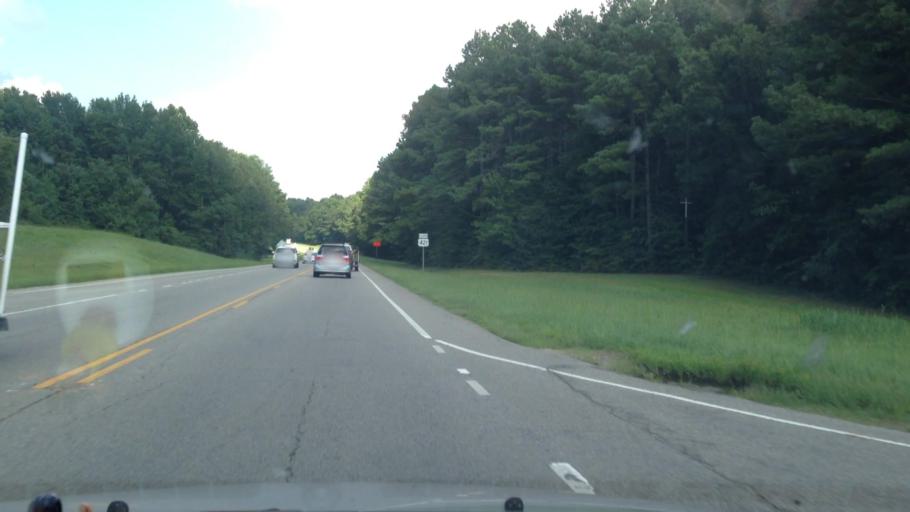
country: US
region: North Carolina
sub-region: Lee County
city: Broadway
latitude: 35.4384
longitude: -79.0669
